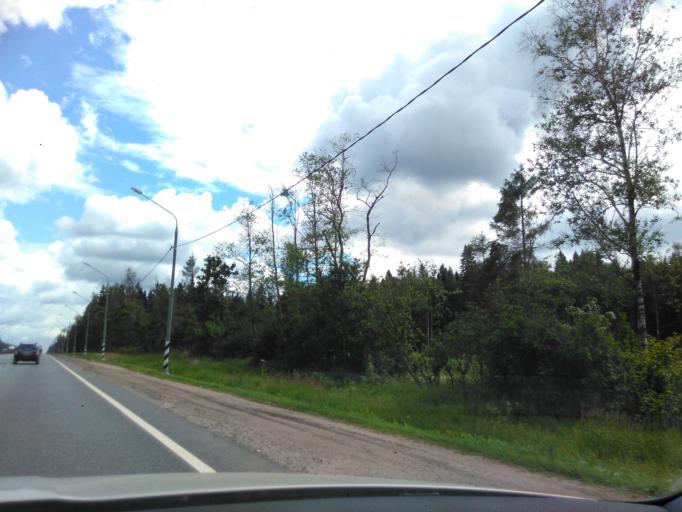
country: RU
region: Moskovskaya
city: Shevlyakovo
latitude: 56.2684
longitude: 36.8469
